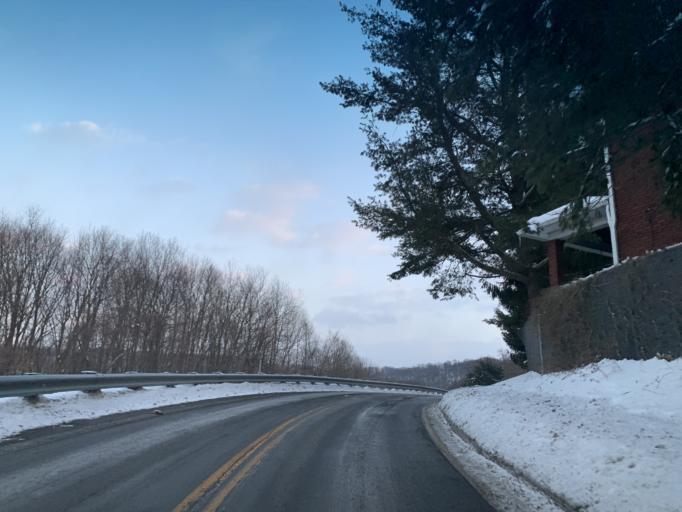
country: US
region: Maryland
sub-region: Allegany County
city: Frostburg
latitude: 39.6629
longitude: -78.9261
